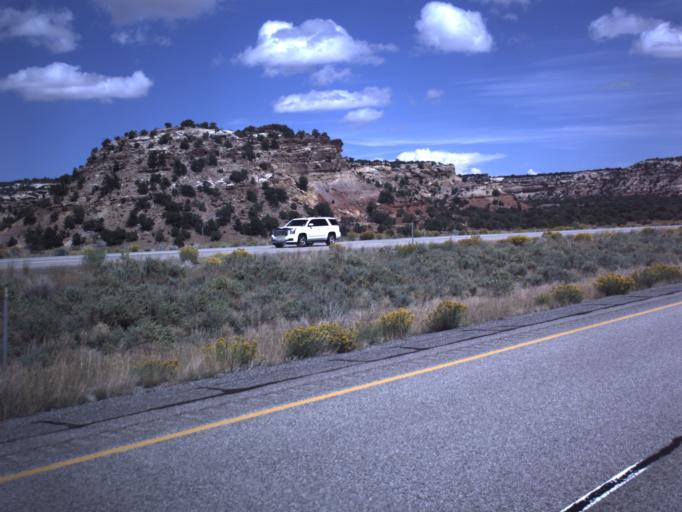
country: US
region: Utah
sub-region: Emery County
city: Castle Dale
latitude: 38.8750
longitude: -110.7457
